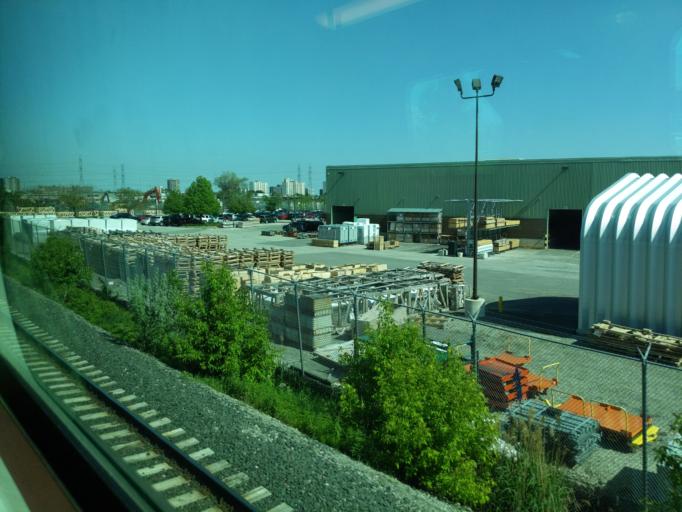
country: CA
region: Ontario
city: Etobicoke
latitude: 43.7061
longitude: -79.5738
